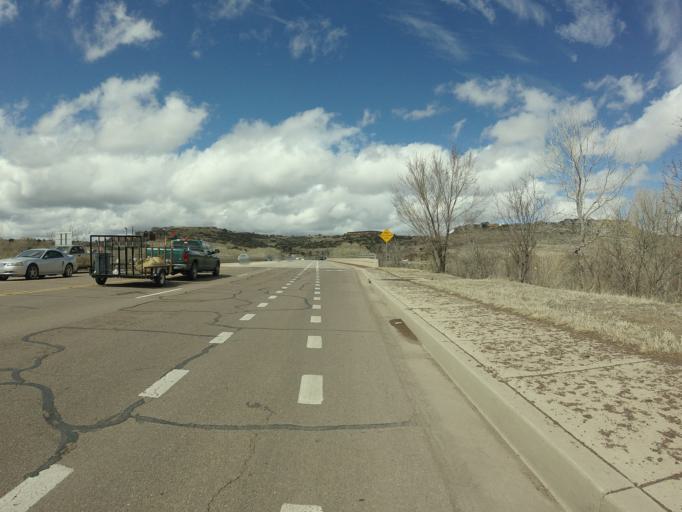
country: US
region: Arizona
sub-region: Yavapai County
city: Prescott
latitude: 34.5755
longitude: -112.4298
